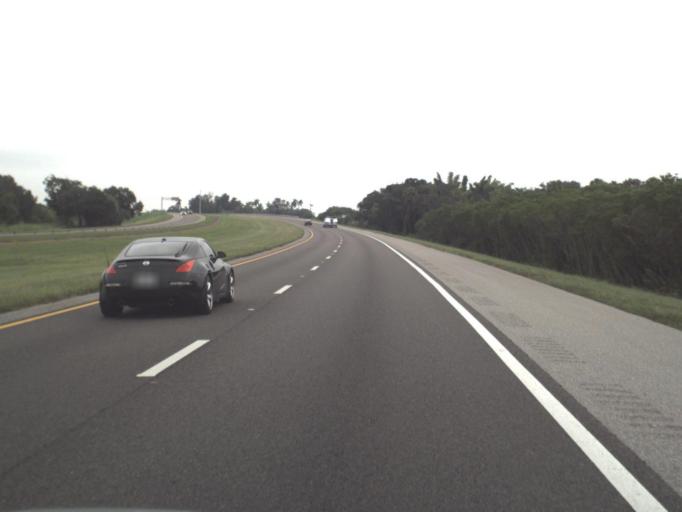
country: US
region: Florida
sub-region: Manatee County
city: Memphis
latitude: 27.5801
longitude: -82.5735
